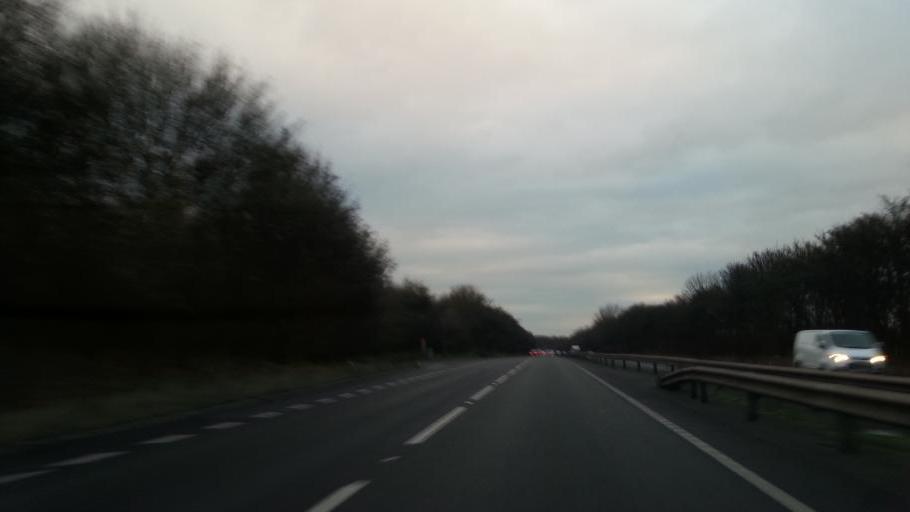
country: GB
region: England
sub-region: Nottinghamshire
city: Newark on Trent
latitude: 53.0719
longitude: -0.7682
